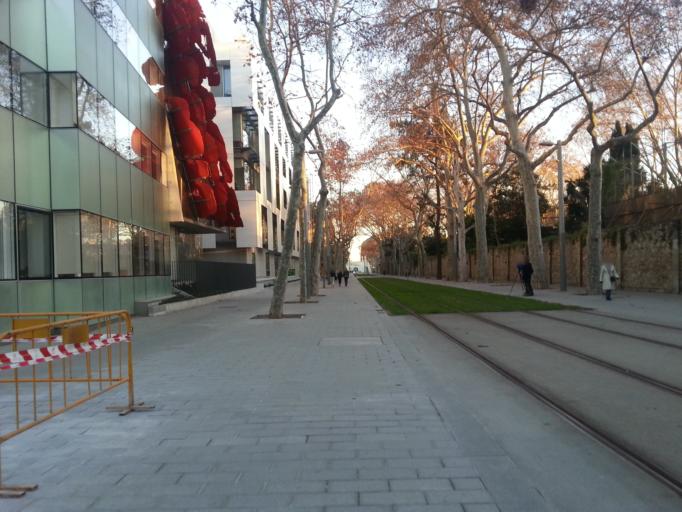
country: ES
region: Catalonia
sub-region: Provincia de Barcelona
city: Ciutat Vella
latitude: 41.3897
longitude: 2.1893
